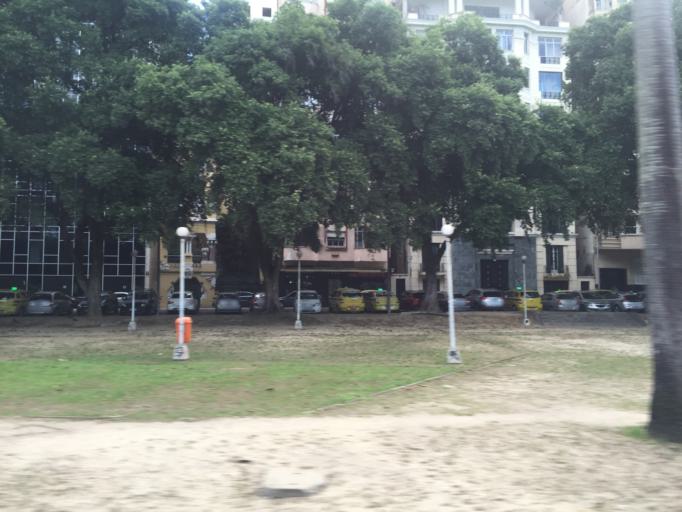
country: BR
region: Rio de Janeiro
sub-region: Rio De Janeiro
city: Rio de Janeiro
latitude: -22.9237
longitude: -43.1724
